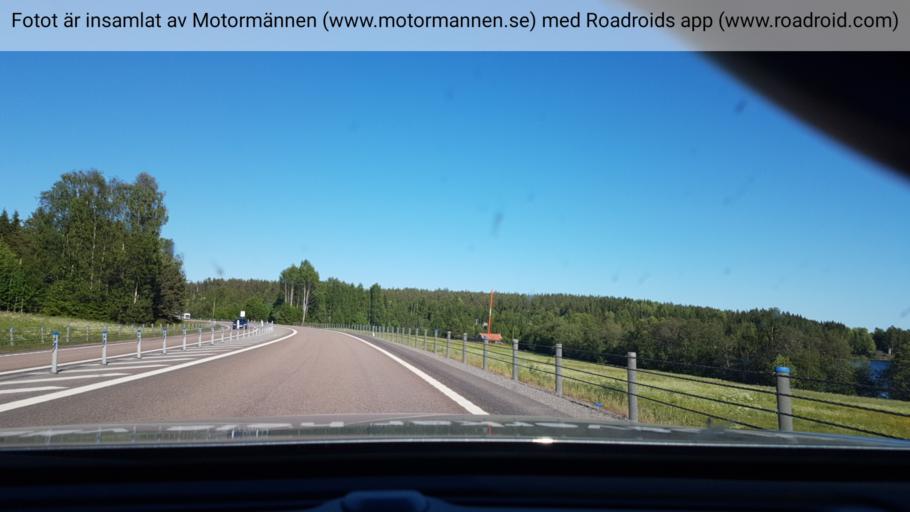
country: SE
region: Vaesternorrland
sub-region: Timra Kommun
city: Soraker
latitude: 62.5576
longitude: 17.6650
